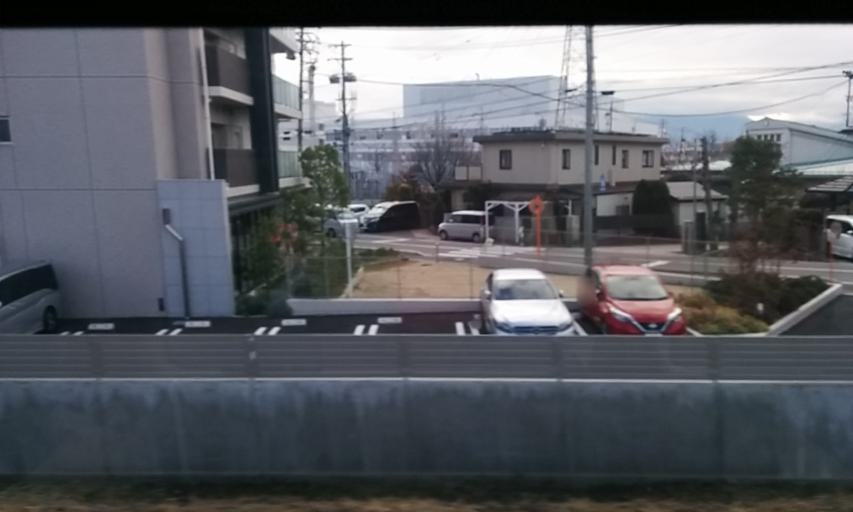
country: JP
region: Nagano
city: Matsumoto
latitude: 36.2390
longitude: 137.9589
